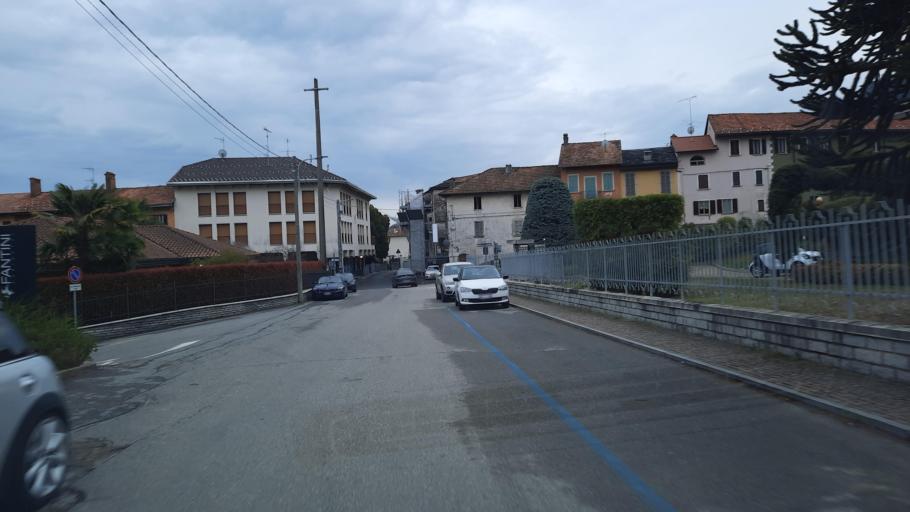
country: IT
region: Piedmont
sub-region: Provincia di Novara
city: Pella
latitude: 45.8023
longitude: 8.3856
